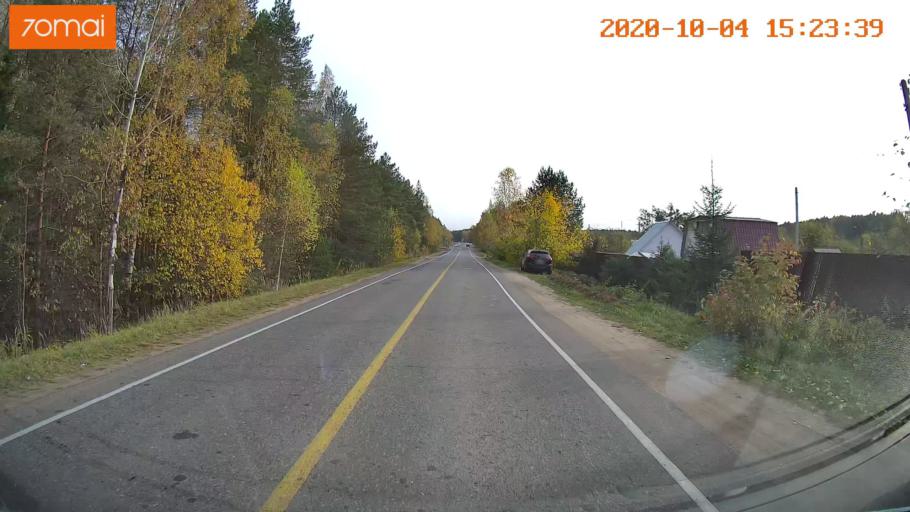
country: RU
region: Ivanovo
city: Bogorodskoye
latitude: 57.0717
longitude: 40.9507
